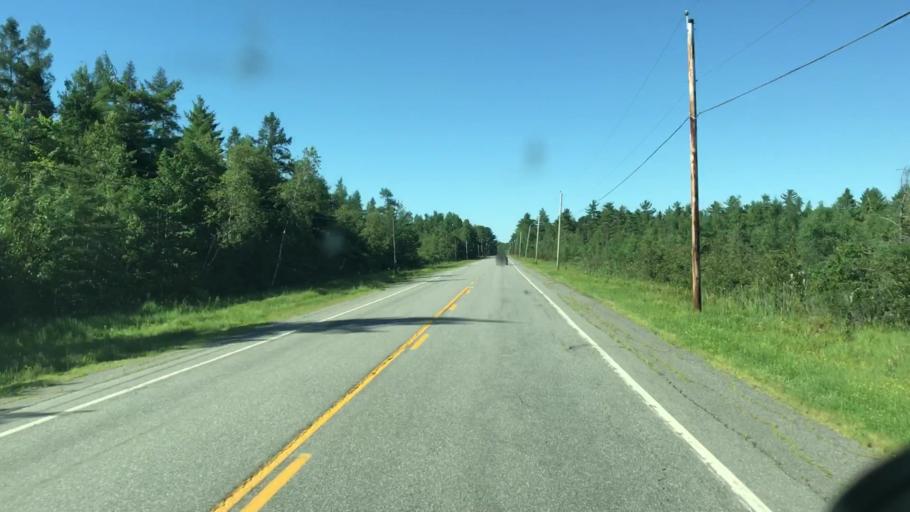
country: US
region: Maine
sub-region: Penobscot County
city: Howland
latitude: 45.2836
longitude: -68.6277
